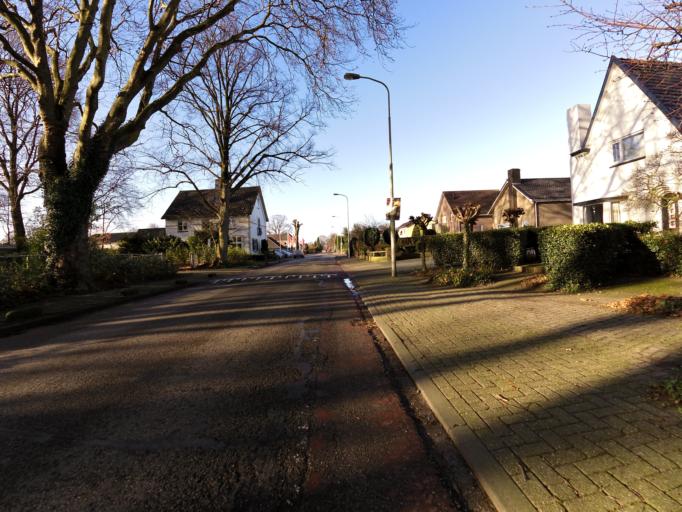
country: NL
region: Gelderland
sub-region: Gemeente Montferland
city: s-Heerenberg
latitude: 51.9204
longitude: 6.1979
